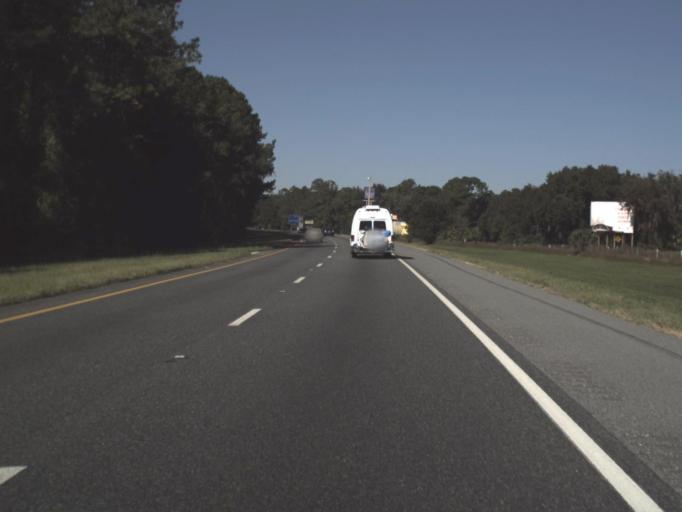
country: US
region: Florida
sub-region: Sumter County
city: Wildwood
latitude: 28.8313
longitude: -82.0341
